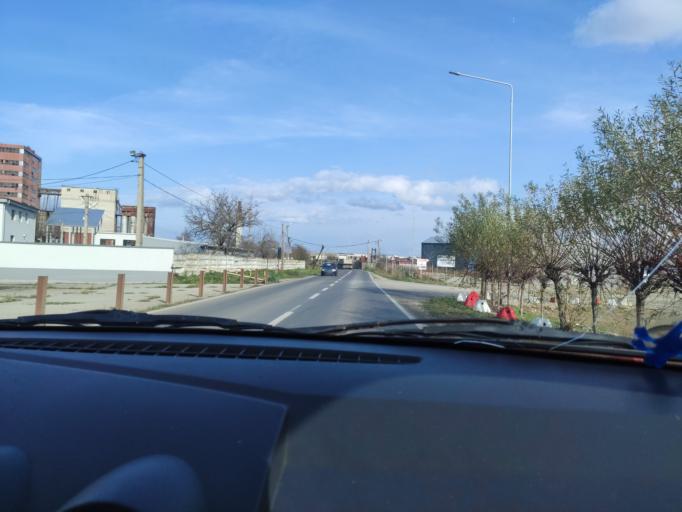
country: RO
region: Brasov
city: Codlea
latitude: 45.7061
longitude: 25.4591
